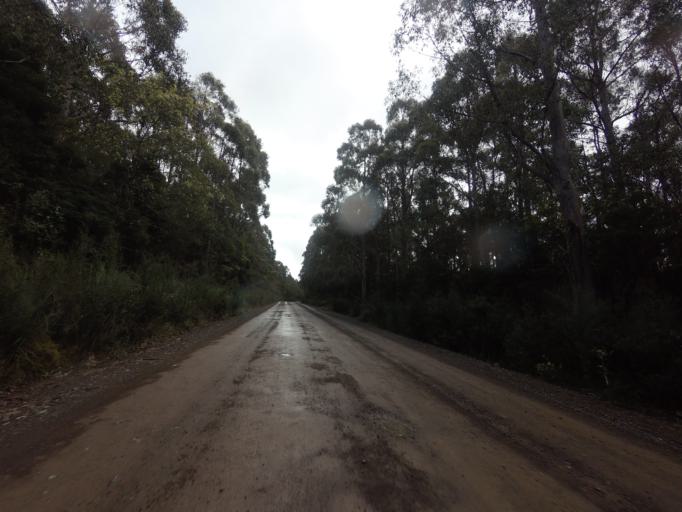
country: AU
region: Tasmania
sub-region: Huon Valley
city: Geeveston
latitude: -43.4644
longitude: 146.8998
